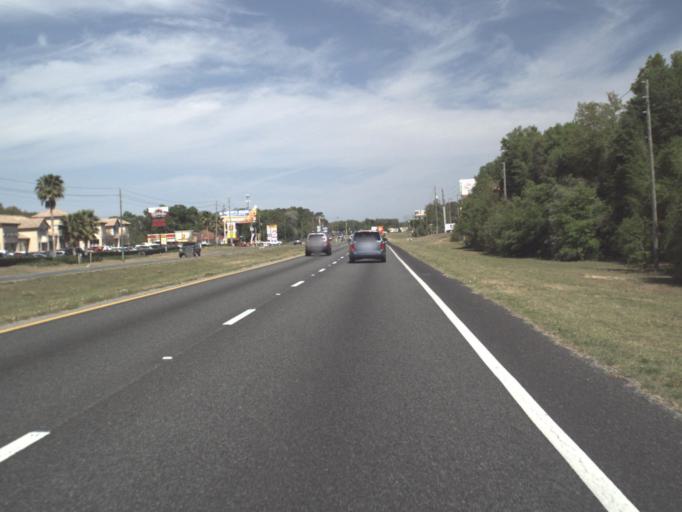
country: US
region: Florida
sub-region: Sumter County
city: The Villages
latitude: 28.9764
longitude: -81.9817
